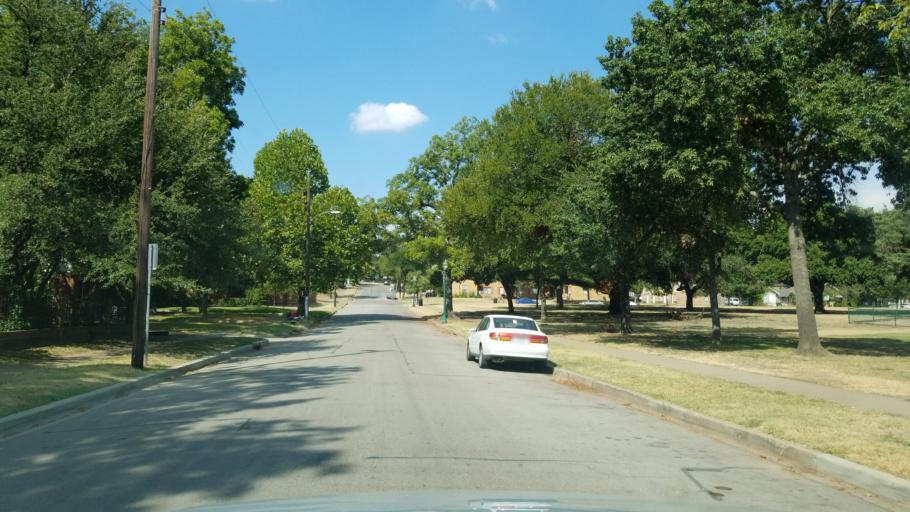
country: US
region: Texas
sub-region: Dallas County
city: Dallas
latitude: 32.7548
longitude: -96.8204
